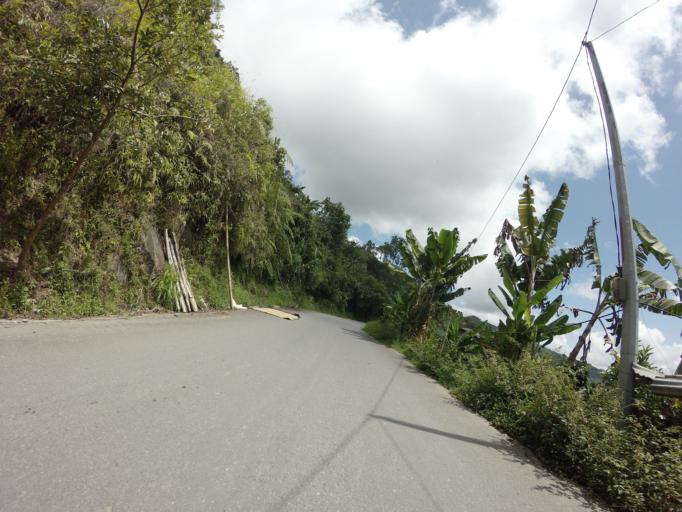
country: CO
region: Caldas
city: Marquetalia
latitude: 5.2951
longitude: -75.0895
